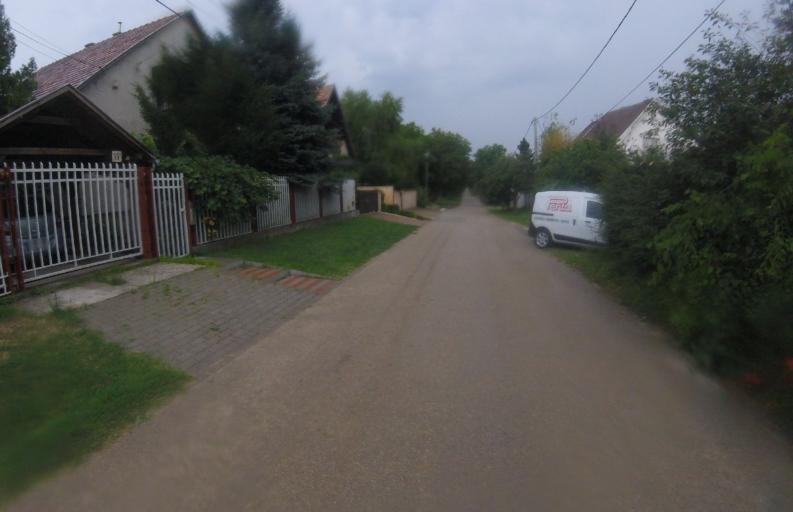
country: HU
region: Pest
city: God
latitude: 47.6732
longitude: 19.1416
